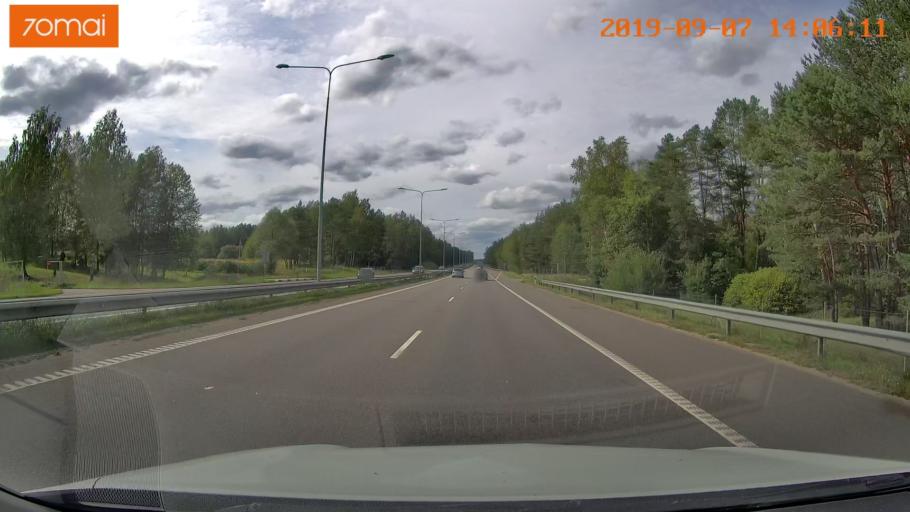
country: LT
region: Vilnius County
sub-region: Vilniaus Rajonas
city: Vievis
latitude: 54.7578
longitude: 24.8901
